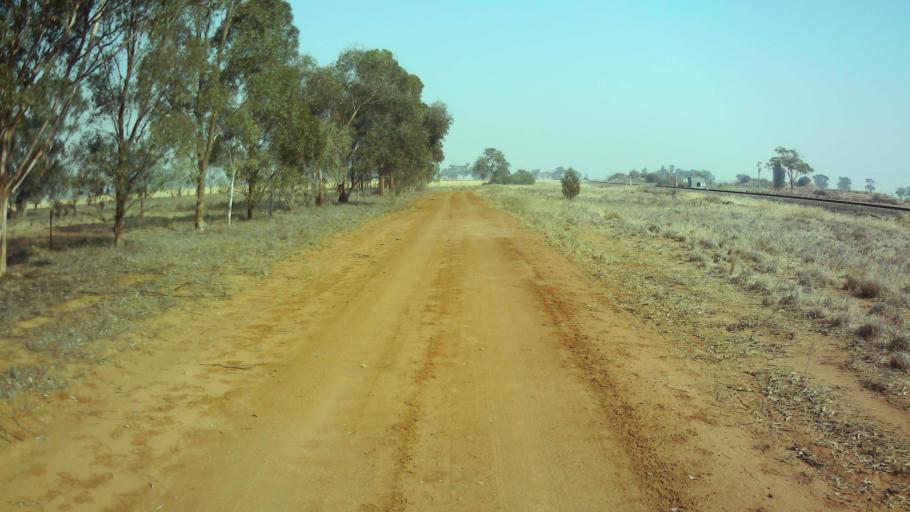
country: AU
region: New South Wales
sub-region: Weddin
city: Grenfell
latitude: -34.0036
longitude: 147.7889
